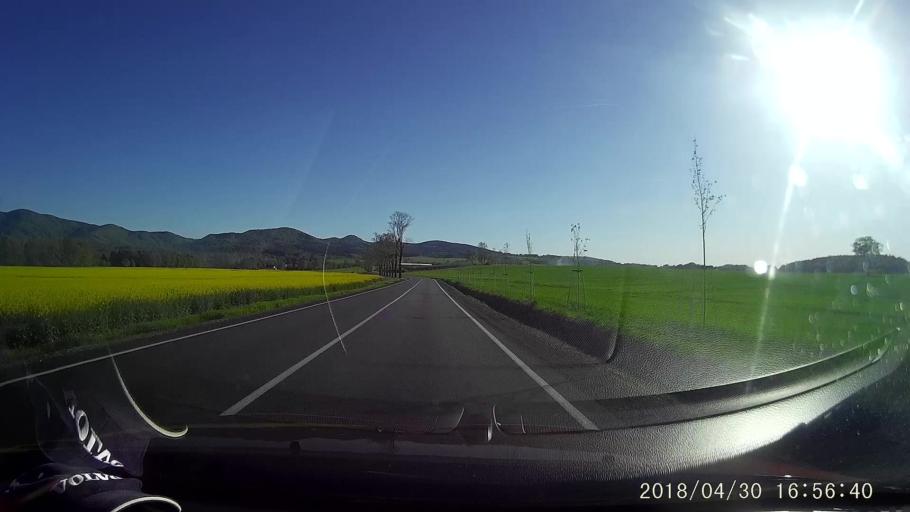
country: CZ
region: Liberecky
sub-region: Okres Liberec
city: Raspenava
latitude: 50.9156
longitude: 15.1226
